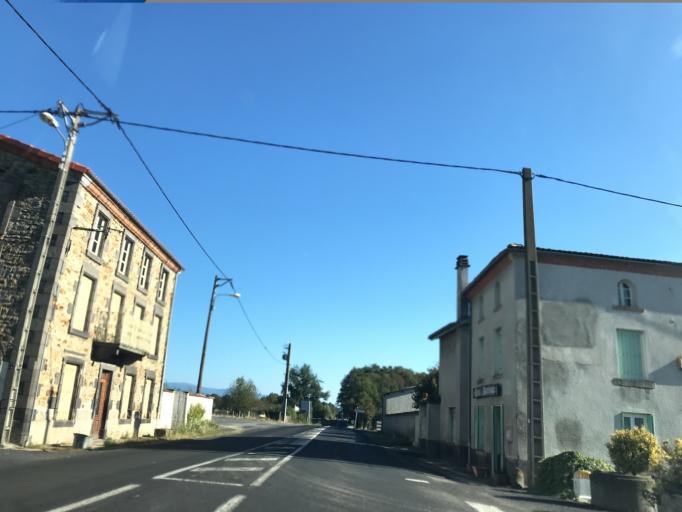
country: FR
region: Auvergne
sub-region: Departement du Puy-de-Dome
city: Peschadoires
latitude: 45.7894
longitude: 3.4610
